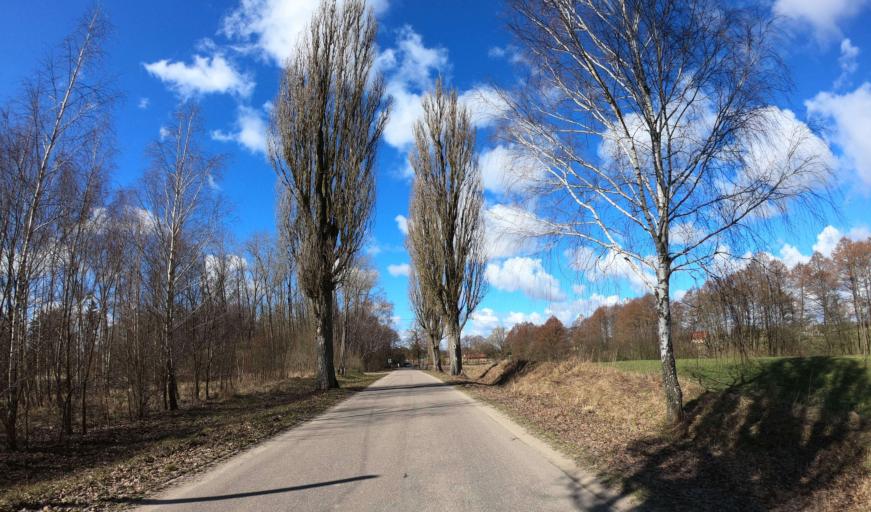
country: PL
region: West Pomeranian Voivodeship
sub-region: Powiat drawski
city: Drawsko Pomorskie
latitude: 53.4877
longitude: 15.8678
